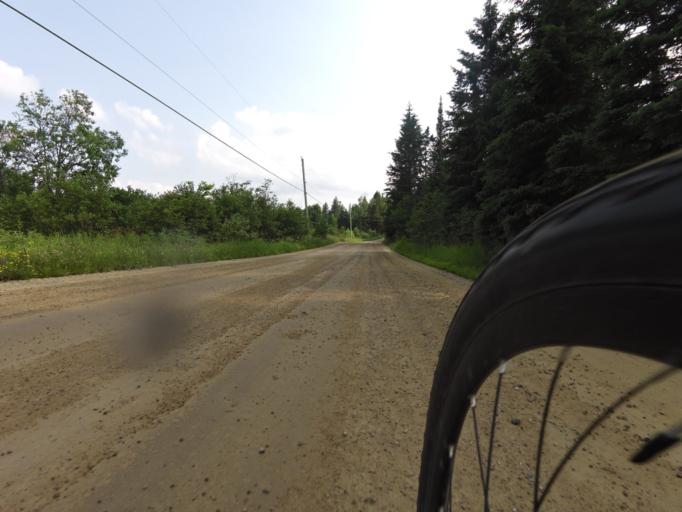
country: CA
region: Quebec
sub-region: Laurentides
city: Mont-Tremblant
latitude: 45.9448
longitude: -74.5950
